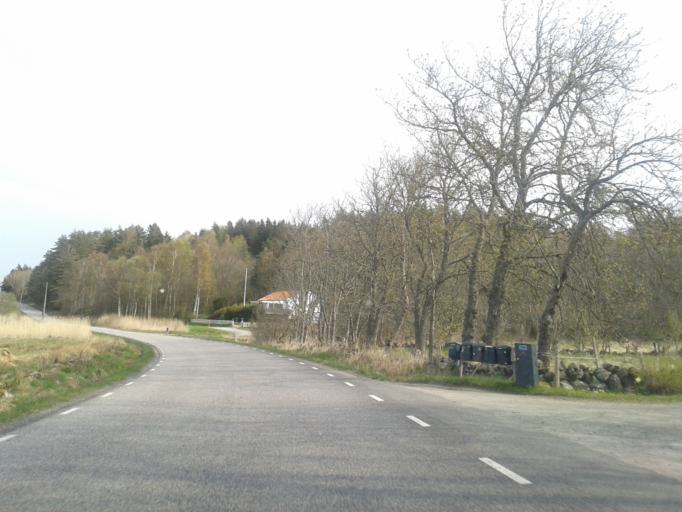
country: SE
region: Vaestra Goetaland
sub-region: Kungalvs Kommun
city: Kode
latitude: 57.9011
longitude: 11.8051
